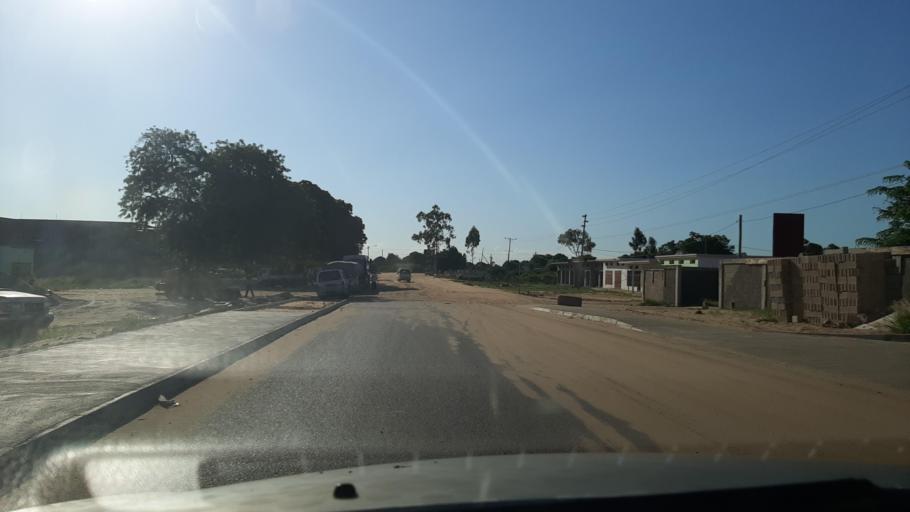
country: MZ
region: Maputo City
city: Maputo
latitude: -25.7531
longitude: 32.5502
